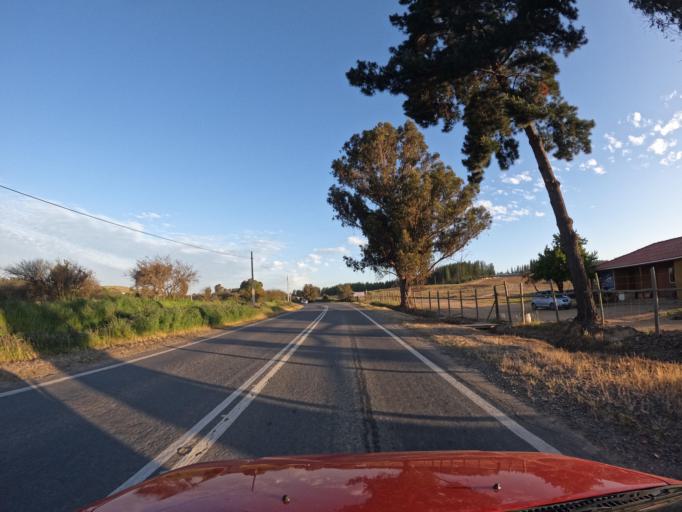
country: CL
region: O'Higgins
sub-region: Provincia de Colchagua
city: Santa Cruz
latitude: -34.3400
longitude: -71.7425
